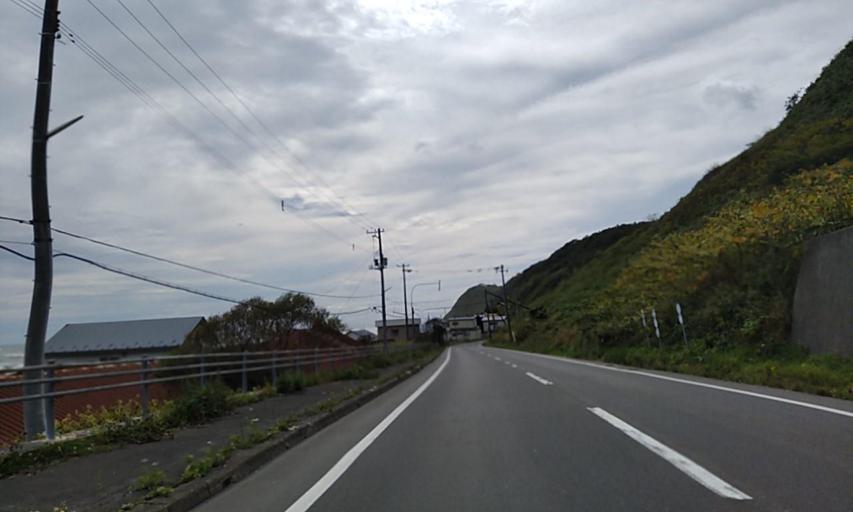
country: JP
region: Hokkaido
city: Kushiro
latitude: 42.8007
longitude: 143.8121
